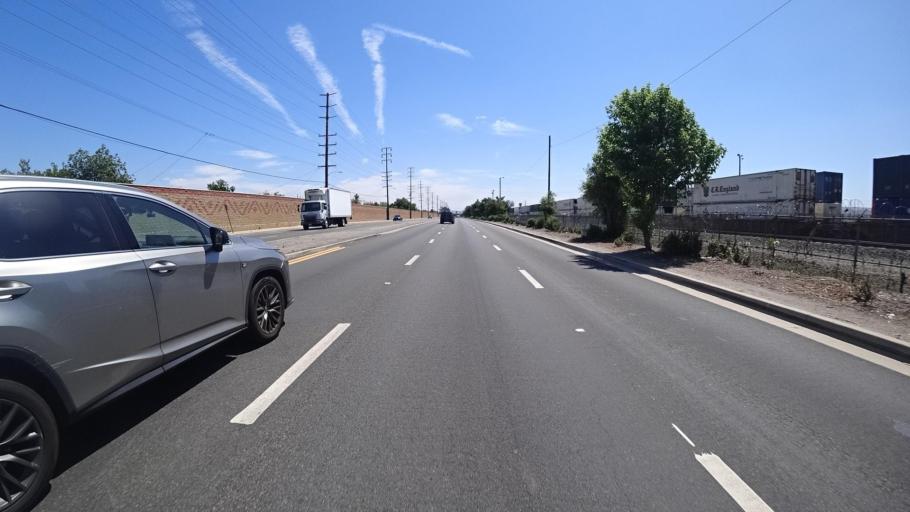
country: US
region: California
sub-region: Los Angeles County
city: La Puente
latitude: 34.0108
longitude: -117.9365
